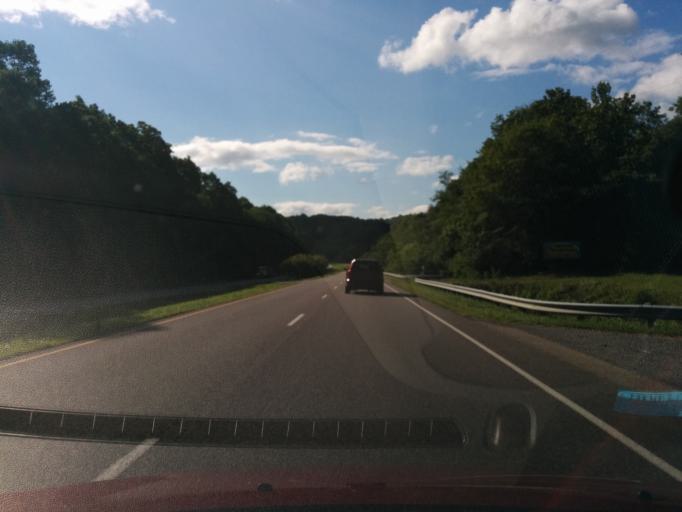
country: US
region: Virginia
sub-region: City of Lexington
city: Lexington
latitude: 37.7635
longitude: -79.4274
